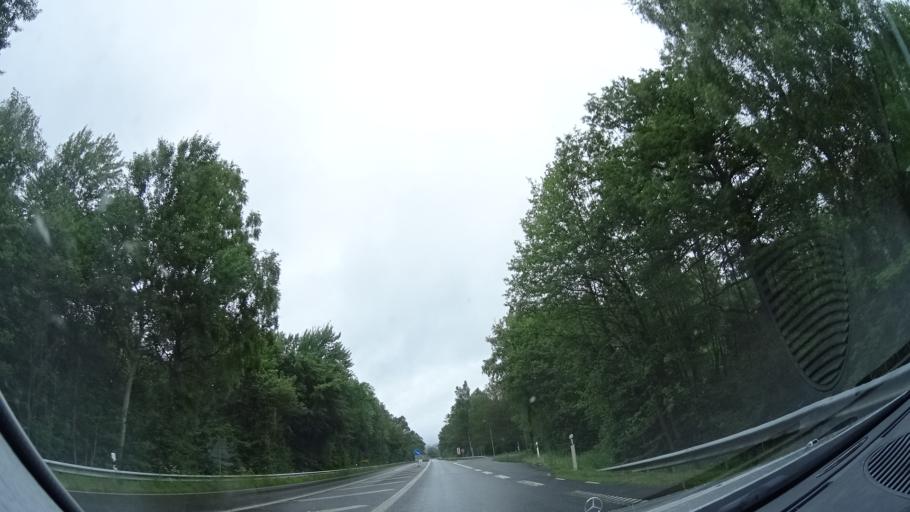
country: SE
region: Skane
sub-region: Hoors Kommun
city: Satofta
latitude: 55.8871
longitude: 13.5227
